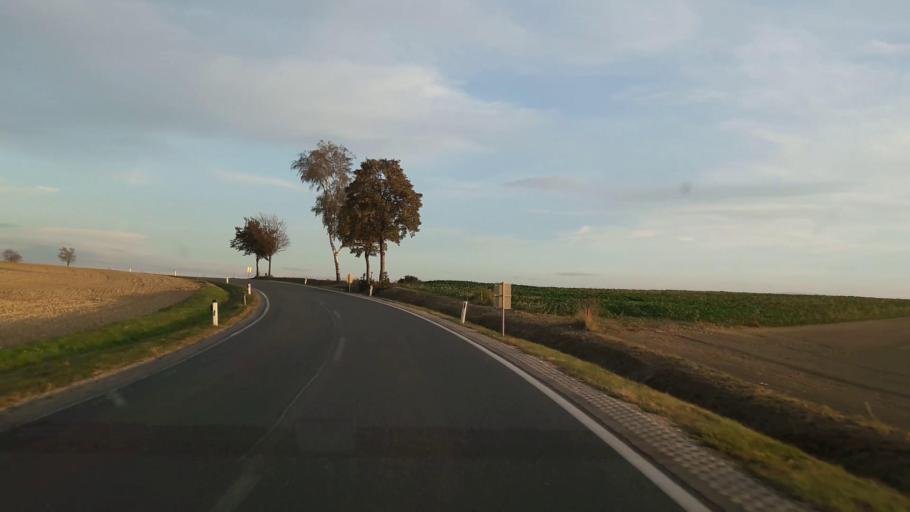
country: AT
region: Lower Austria
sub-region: Politischer Bezirk Korneuburg
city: Grossrussbach
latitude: 48.4539
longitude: 16.3736
